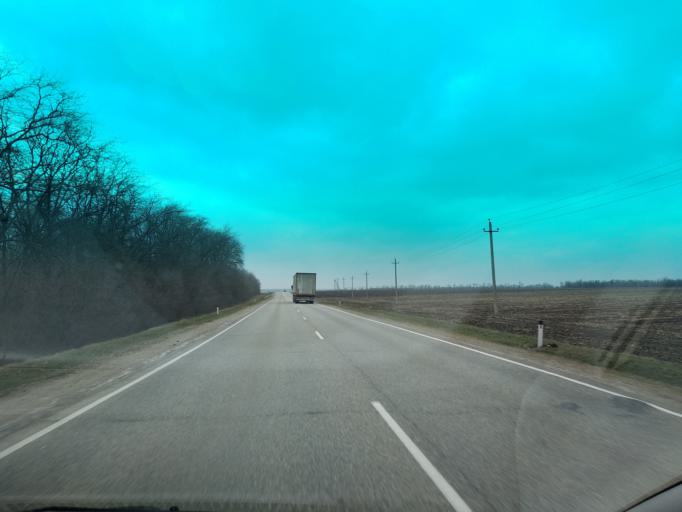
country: RU
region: Krasnodarskiy
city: Novomalorossiyskaya
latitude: 45.7237
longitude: 39.8931
